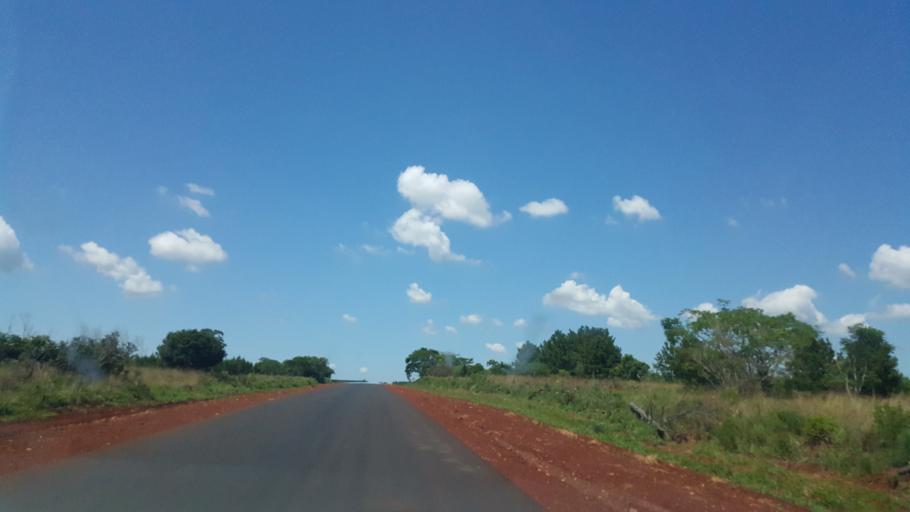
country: AR
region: Corrientes
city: Santo Tome
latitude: -28.4796
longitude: -56.0355
